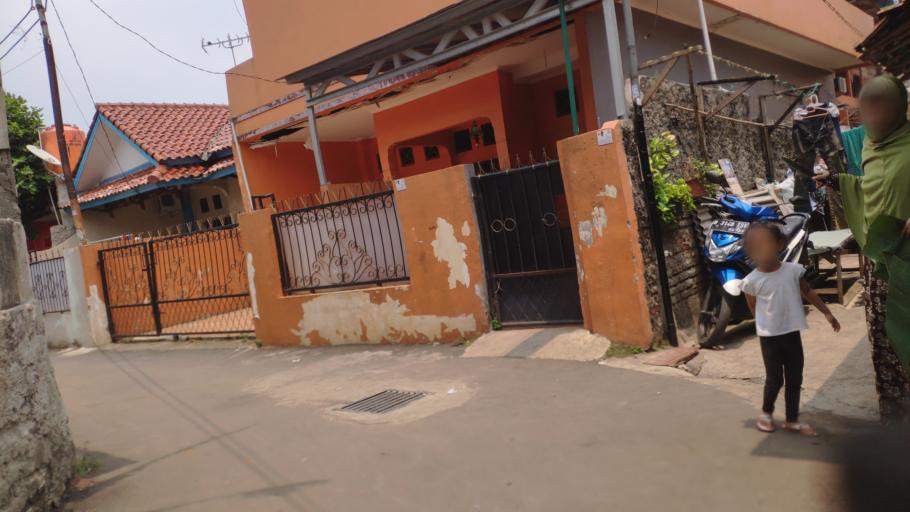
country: ID
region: West Java
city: Depok
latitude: -6.3098
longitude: 106.8324
